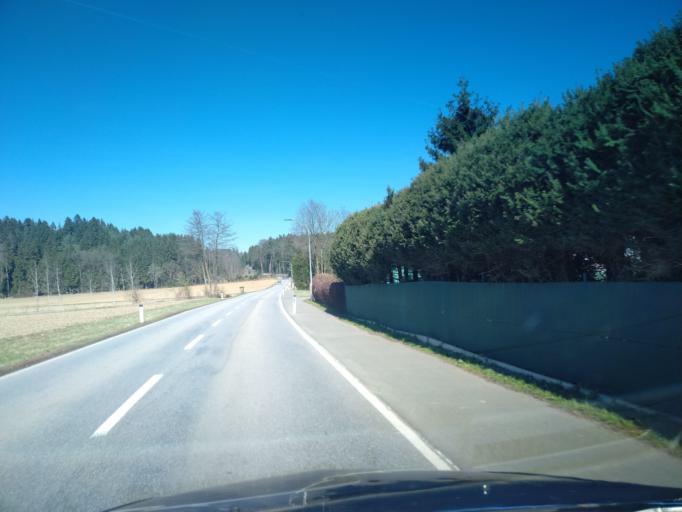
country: AT
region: Styria
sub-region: Politischer Bezirk Graz-Umgebung
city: Zettling
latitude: 46.9130
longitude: 15.4156
